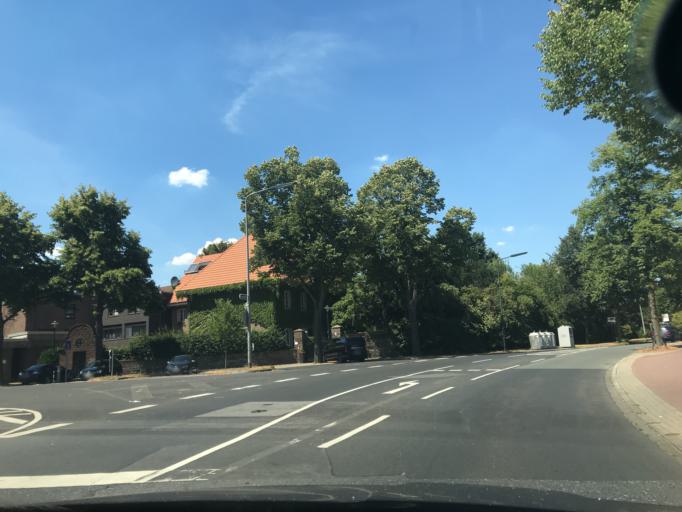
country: DE
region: North Rhine-Westphalia
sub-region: Regierungsbezirk Dusseldorf
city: Dusseldorf
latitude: 51.2740
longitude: 6.7916
